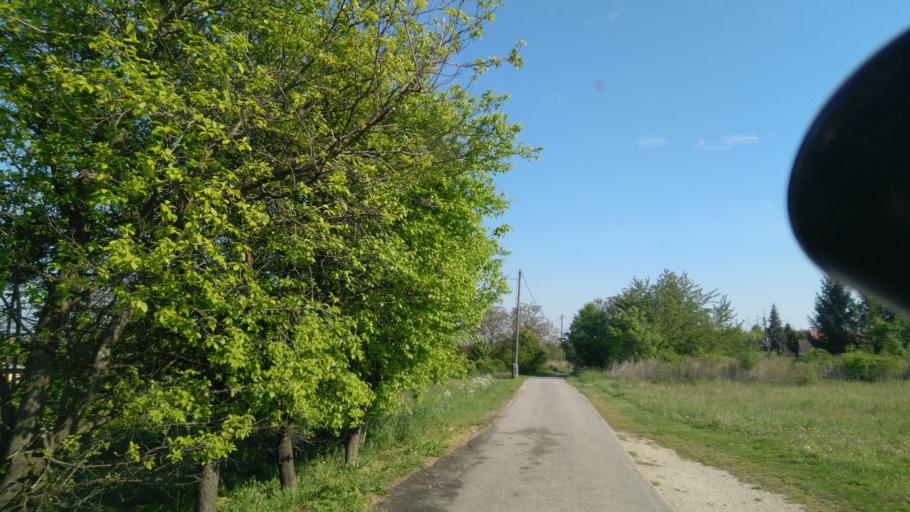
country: HU
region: Zala
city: Sarmellek
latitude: 46.7570
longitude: 17.1415
